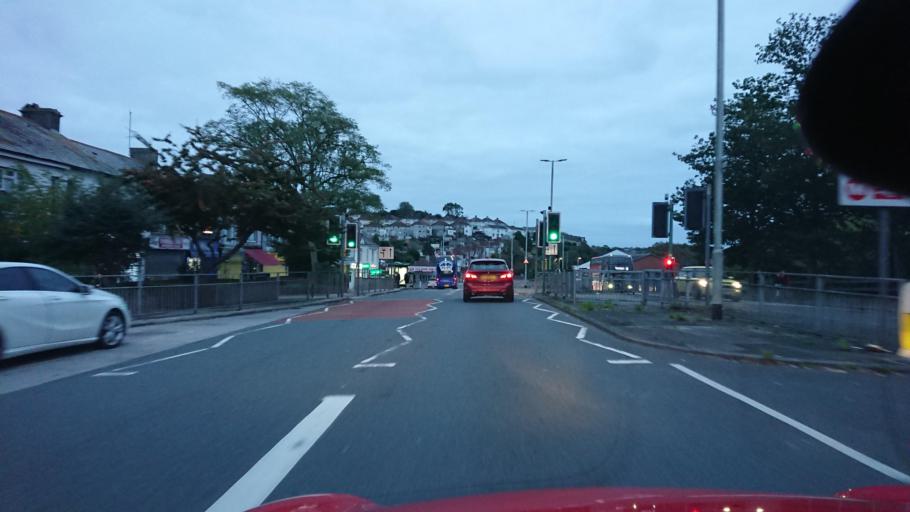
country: GB
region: England
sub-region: Cornwall
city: Torpoint
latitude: 50.4020
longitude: -4.1864
